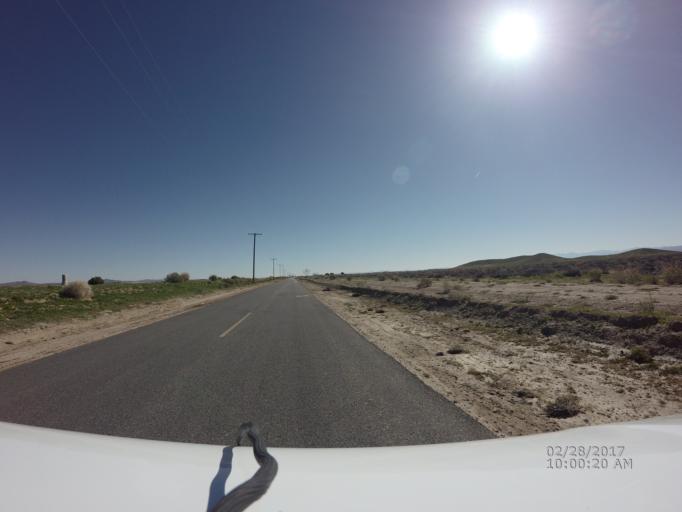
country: US
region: California
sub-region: Kern County
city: Rosamond
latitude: 34.8054
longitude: -118.3124
